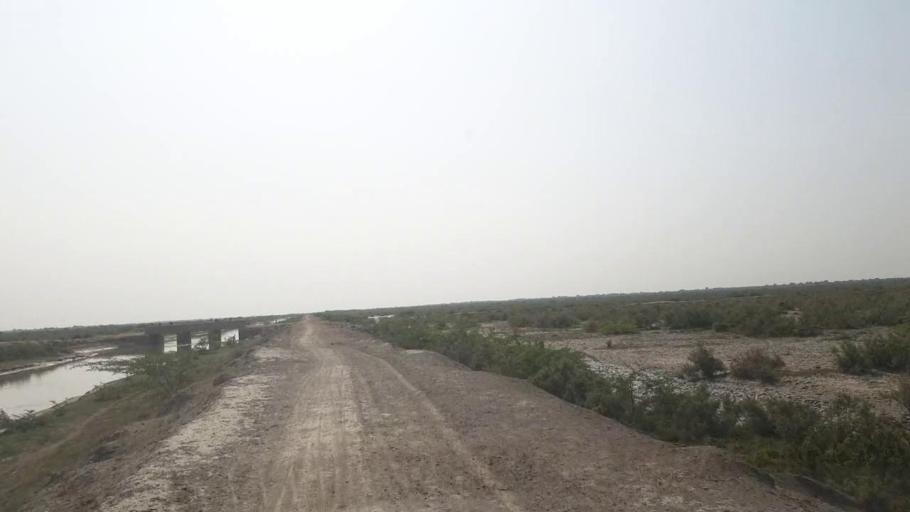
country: PK
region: Sindh
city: Kadhan
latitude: 24.3811
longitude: 68.8979
